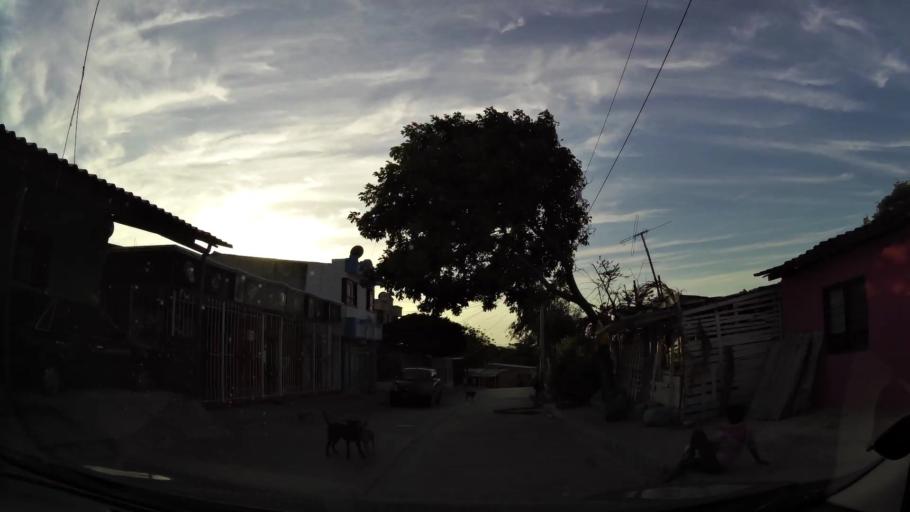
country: CO
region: Atlantico
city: Barranquilla
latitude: 10.9596
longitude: -74.8243
